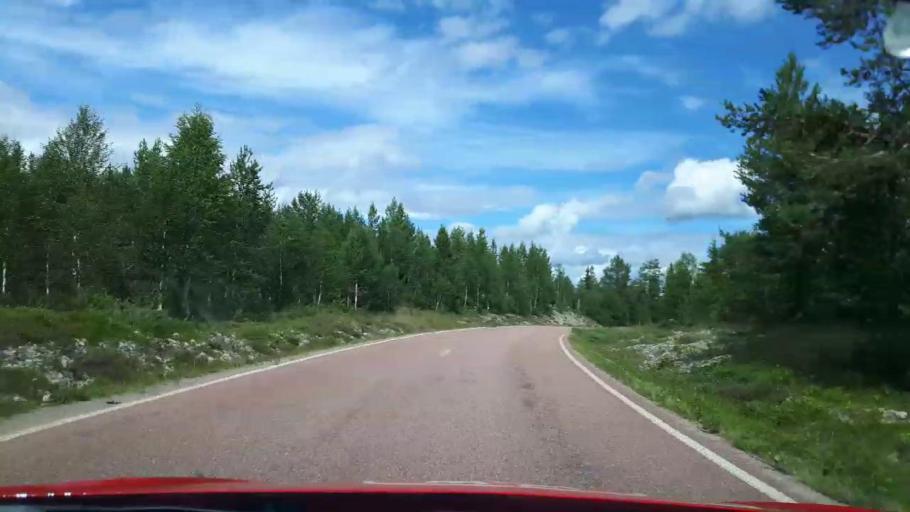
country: NO
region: Hedmark
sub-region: Trysil
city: Innbygda
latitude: 62.0129
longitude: 12.9760
